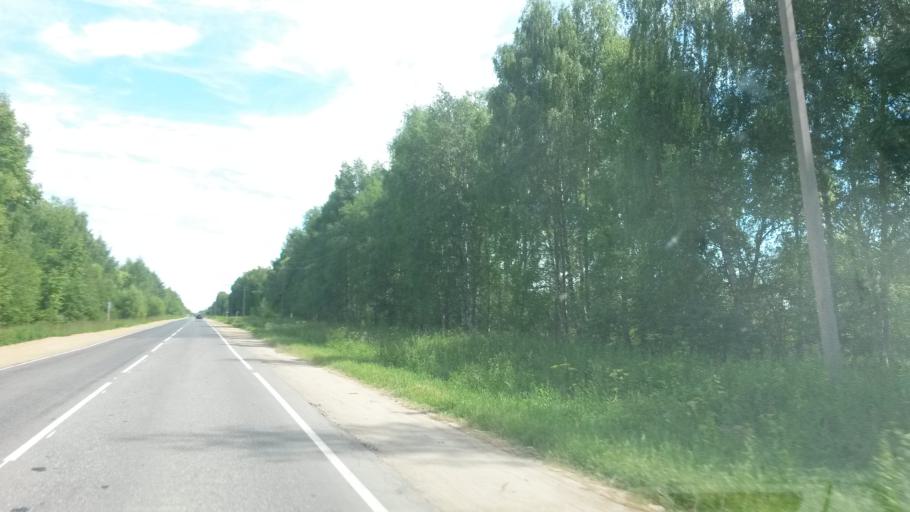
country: RU
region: Ivanovo
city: Zavolzhsk
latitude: 57.5077
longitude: 42.0922
